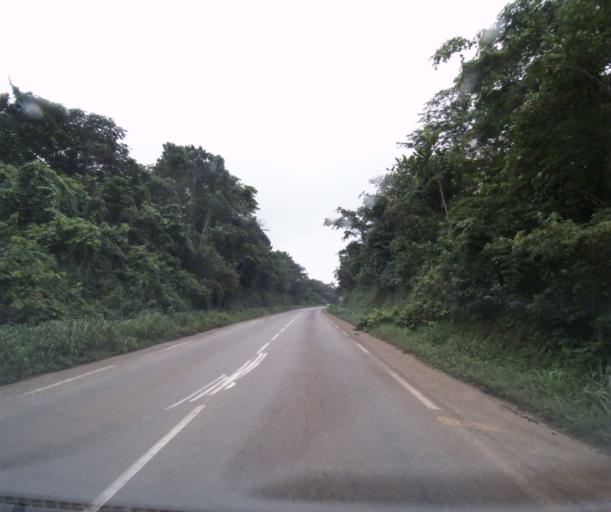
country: CM
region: Centre
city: Eseka
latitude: 3.8714
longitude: 10.6586
